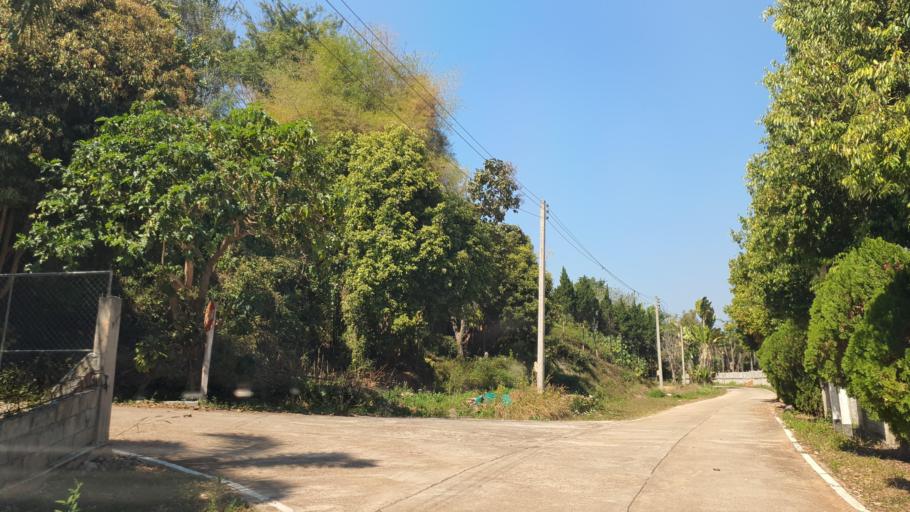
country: TH
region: Lampang
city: Wang Nuea
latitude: 19.1853
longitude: 99.5001
